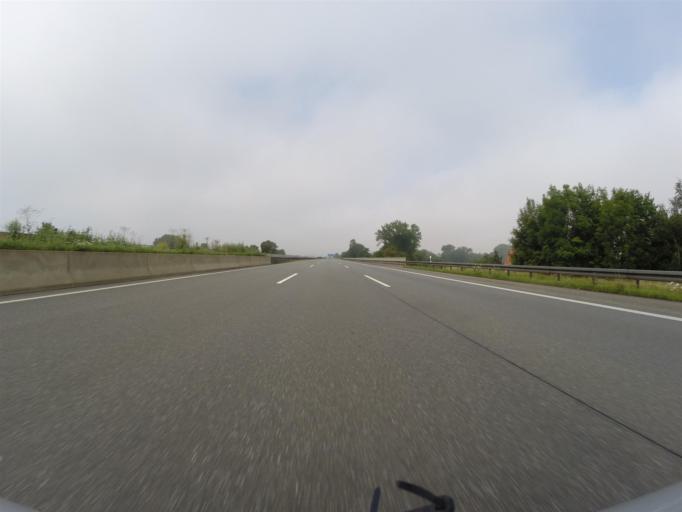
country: DE
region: Thuringia
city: Ernstroda
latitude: 50.9071
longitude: 10.6352
